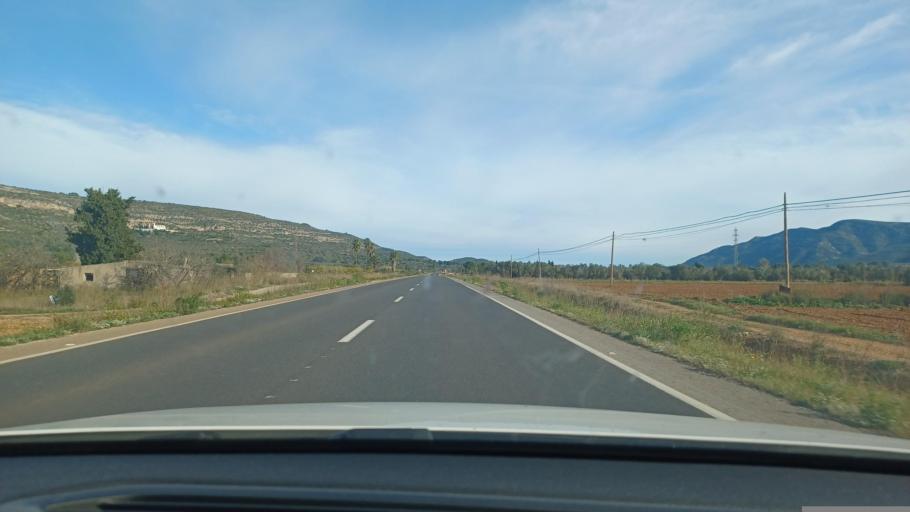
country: ES
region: Catalonia
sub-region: Provincia de Tarragona
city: Ulldecona
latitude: 40.6155
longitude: 0.4669
